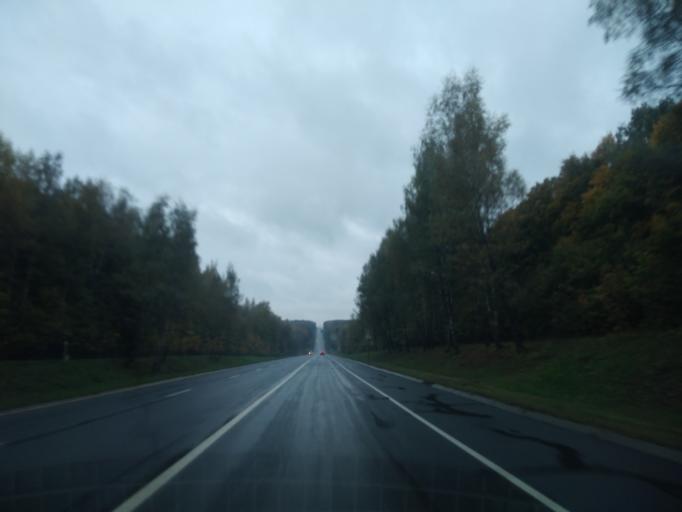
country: RU
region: Tula
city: Barsuki
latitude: 54.2810
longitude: 37.5368
